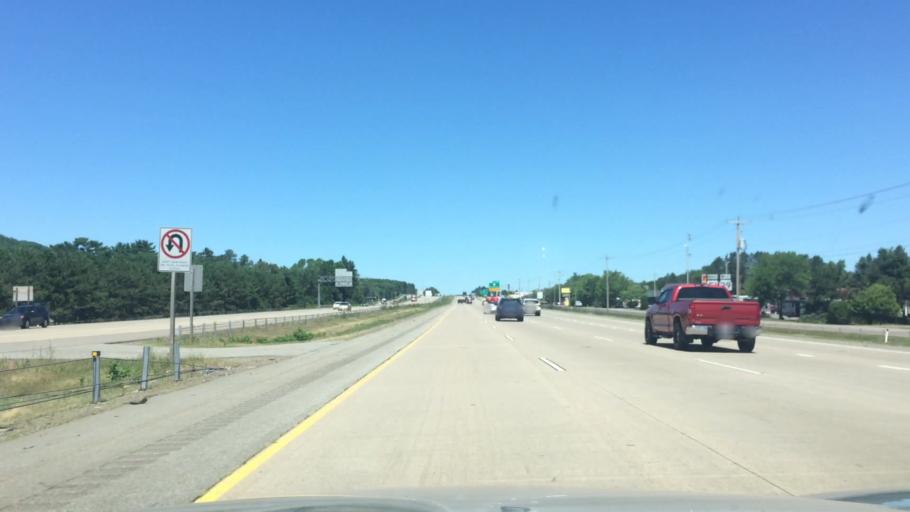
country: US
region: Wisconsin
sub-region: Marathon County
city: Rib Mountain
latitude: 44.9056
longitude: -89.6463
